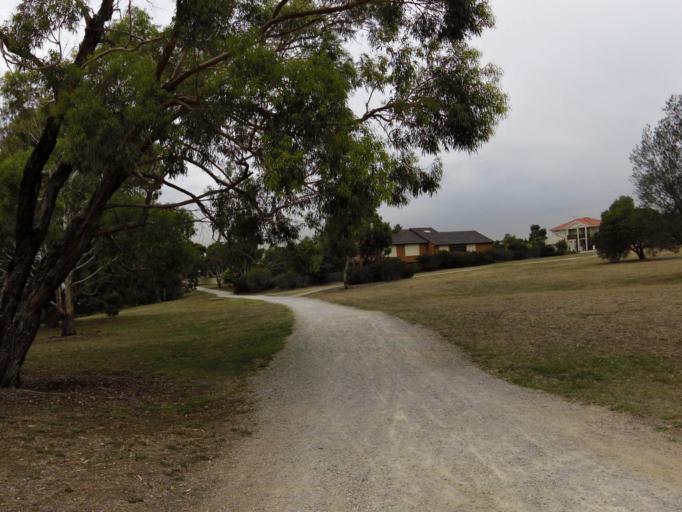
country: AU
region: Victoria
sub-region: Brimbank
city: Taylors Lakes
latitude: -37.7037
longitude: 144.7942
